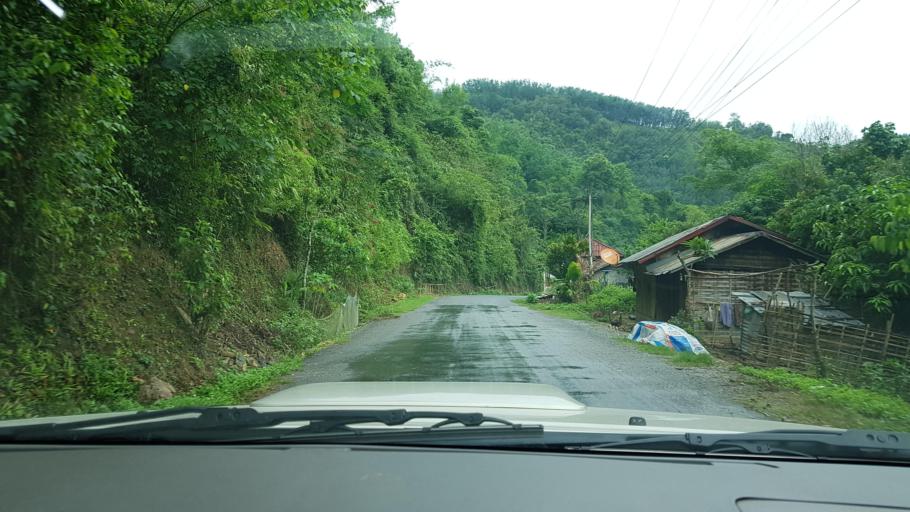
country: LA
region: Phongsali
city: Khoa
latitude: 21.1025
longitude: 102.2832
